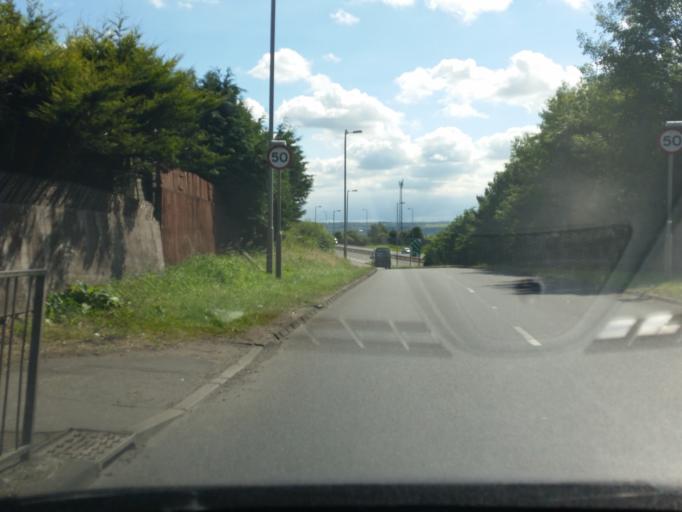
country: GB
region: Scotland
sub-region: North Lanarkshire
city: Bellshill
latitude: 55.8202
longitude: -4.0389
